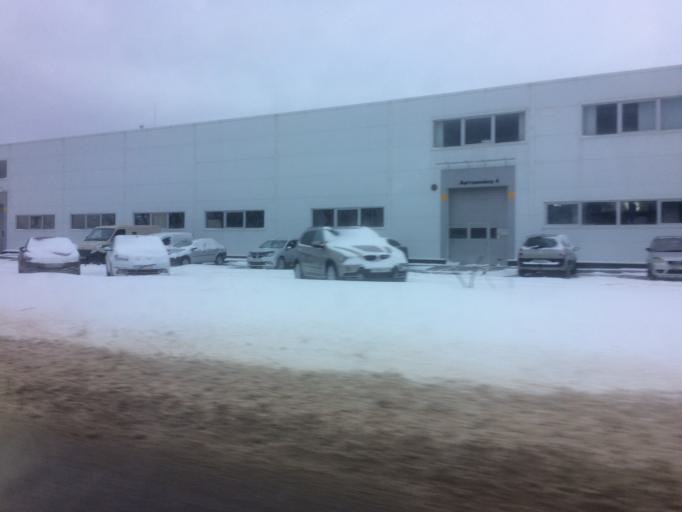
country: RU
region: Tula
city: Tula
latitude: 54.1585
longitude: 37.6373
